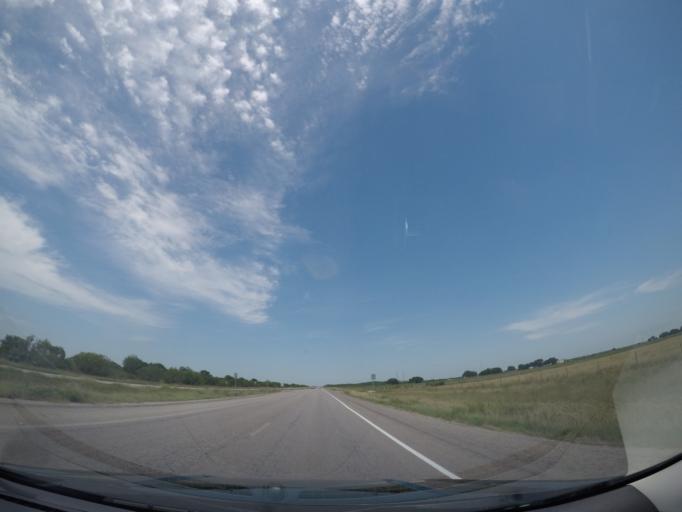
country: US
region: Texas
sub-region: Medina County
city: Hondo
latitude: 29.3495
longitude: -99.1006
